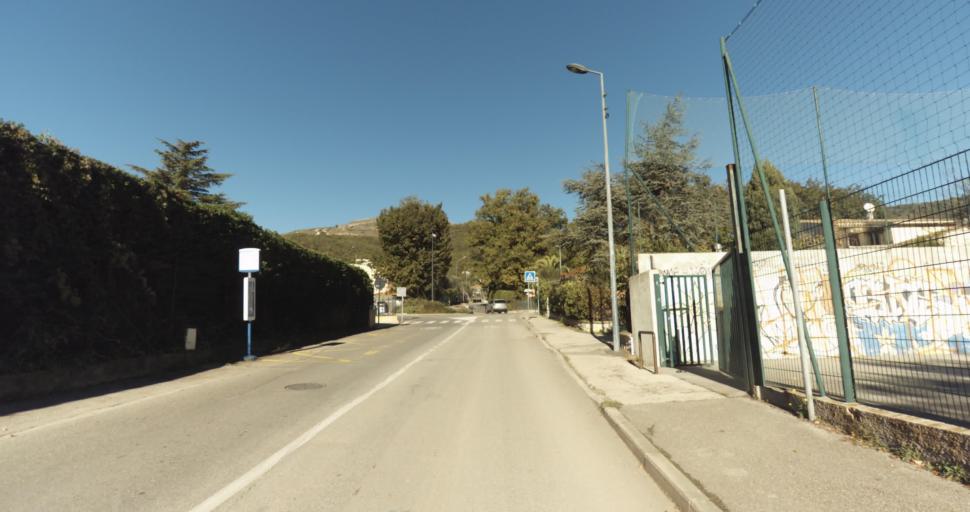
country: FR
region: Provence-Alpes-Cote d'Azur
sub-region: Departement des Alpes-Maritimes
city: Vence
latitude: 43.7203
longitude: 7.0843
